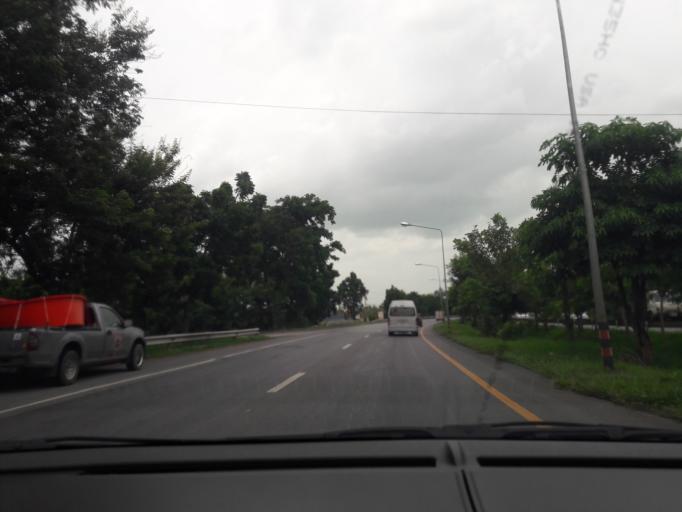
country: TH
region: Nakhon Ratchasima
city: Non Sung
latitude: 15.0973
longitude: 102.2558
